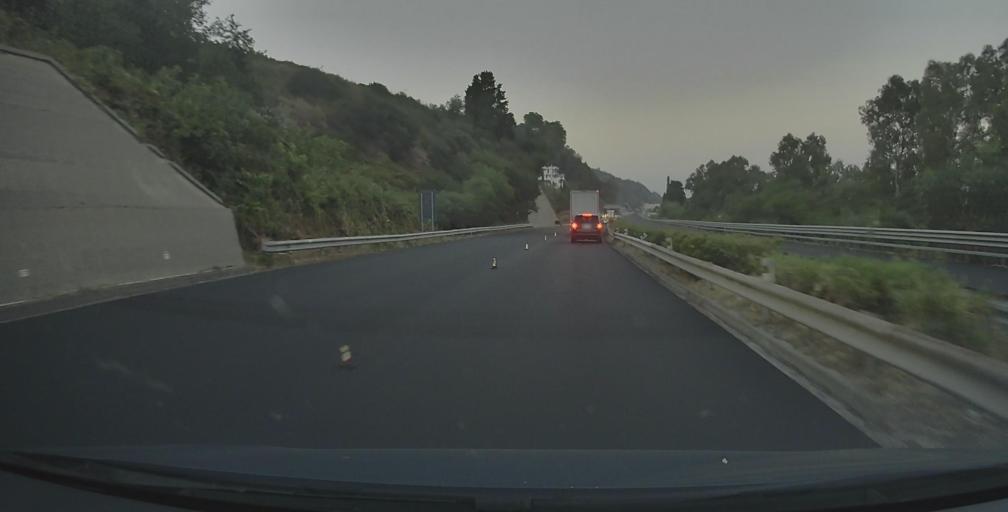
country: IT
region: Sicily
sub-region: Messina
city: Guidomandri Marina
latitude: 38.0380
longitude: 15.4525
